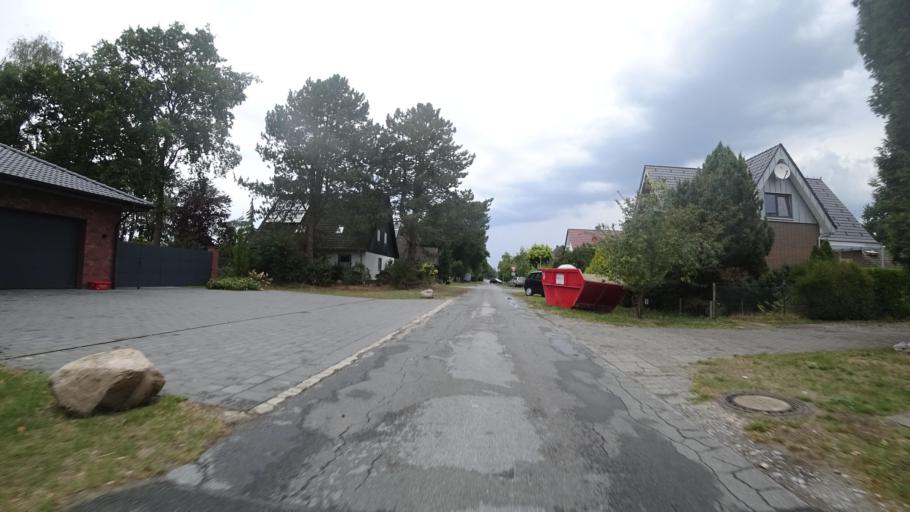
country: DE
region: North Rhine-Westphalia
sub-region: Regierungsbezirk Detmold
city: Rheda-Wiedenbruck
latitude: 51.8925
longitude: 8.2952
